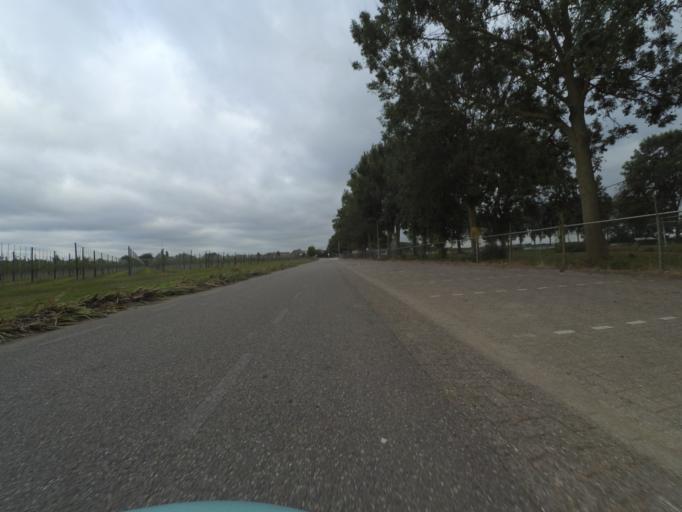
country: NL
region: Gelderland
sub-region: Gemeente Buren
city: Lienden
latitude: 51.9617
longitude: 5.4921
